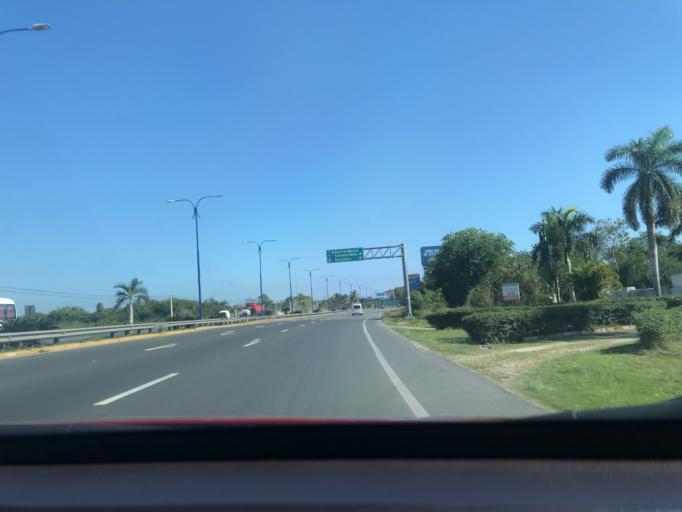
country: DO
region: Santo Domingo
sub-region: Santo Domingo
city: Boca Chica
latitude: 18.4533
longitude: -69.5998
